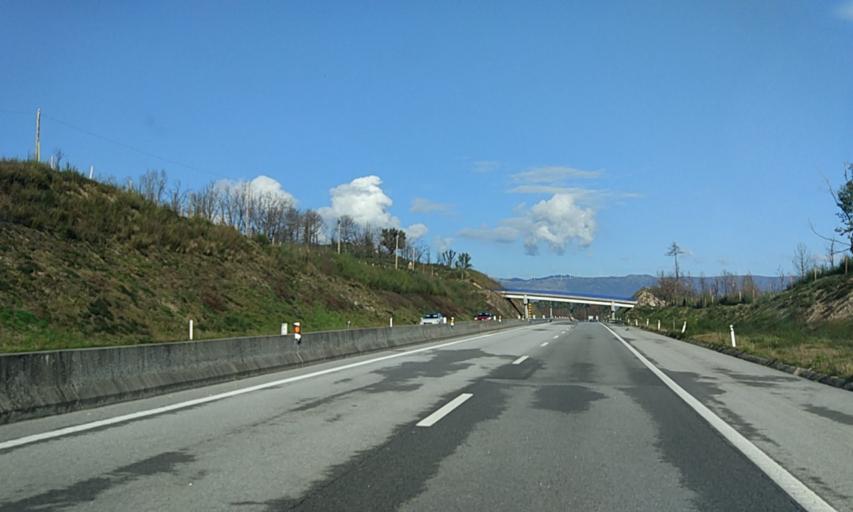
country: PT
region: Viseu
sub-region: Vouzela
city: Vouzela
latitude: 40.7024
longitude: -8.1096
